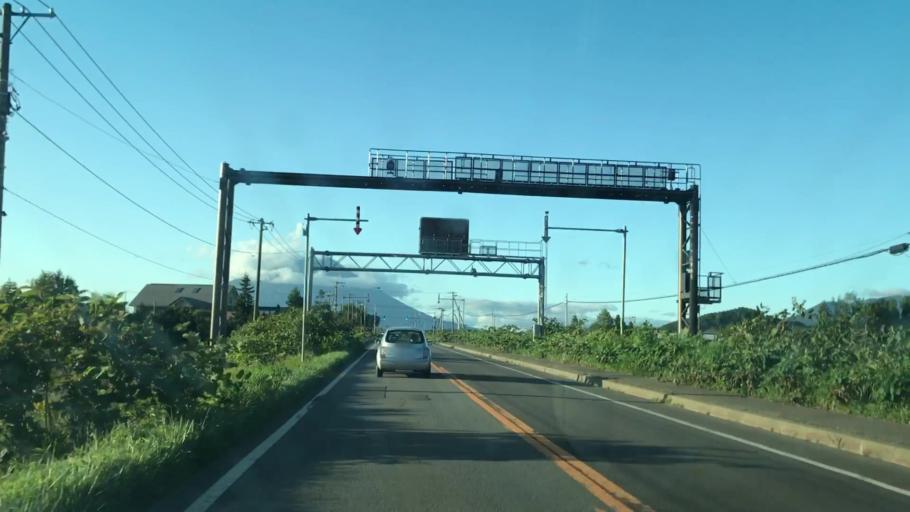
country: JP
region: Hokkaido
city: Niseko Town
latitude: 42.6718
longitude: 140.8423
